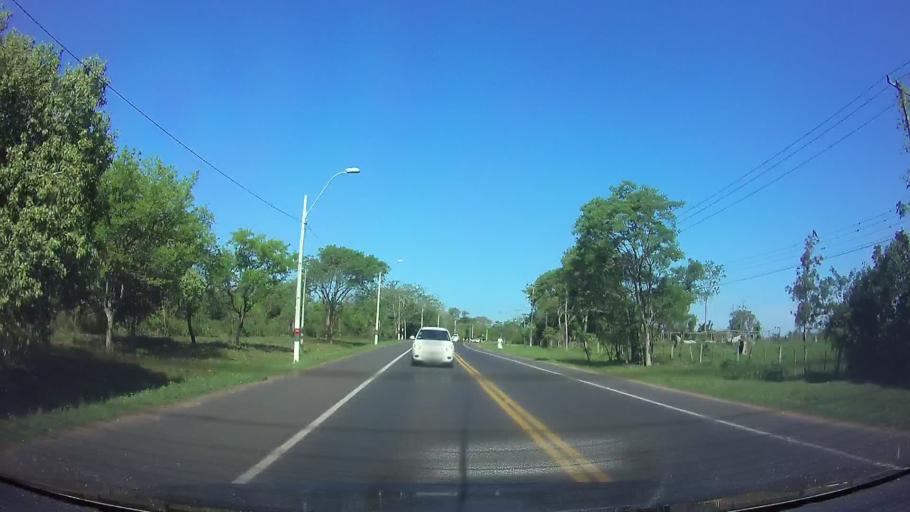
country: PY
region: Central
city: Aregua
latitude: -25.3251
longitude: -57.3644
